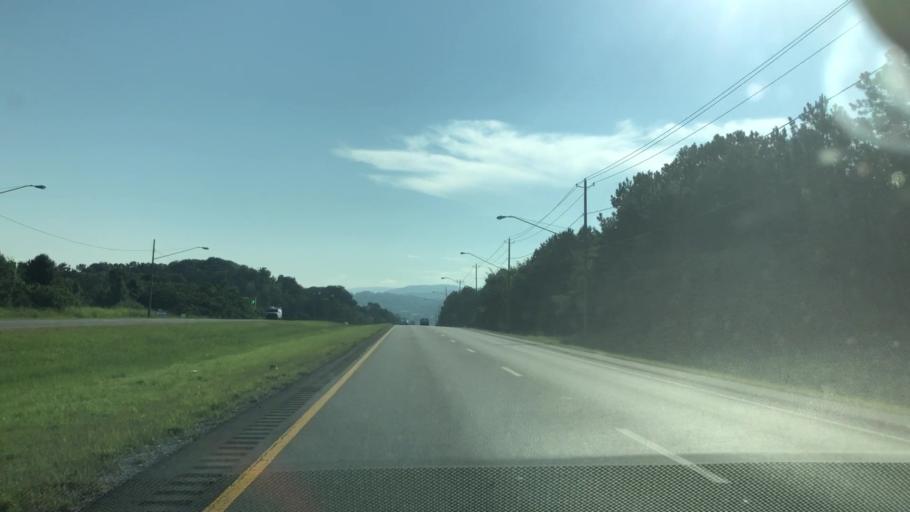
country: US
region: Alabama
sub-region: Calhoun County
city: Anniston
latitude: 33.6525
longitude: -85.8442
